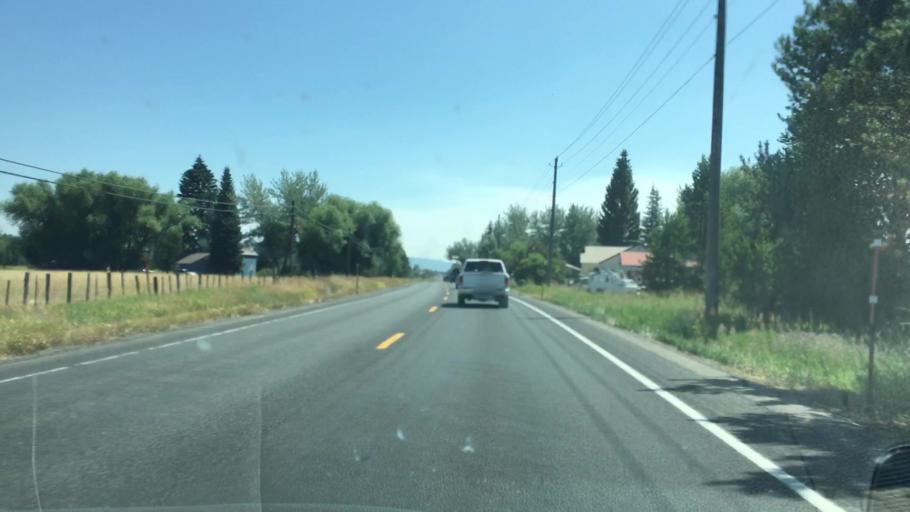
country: US
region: Idaho
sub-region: Valley County
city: McCall
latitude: 44.8503
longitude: -116.0907
